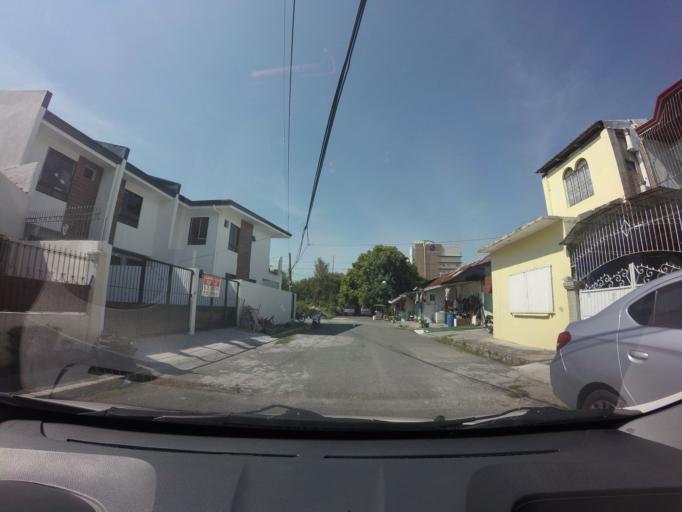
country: PH
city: Sambayanihan People's Village
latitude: 14.4423
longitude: 120.9953
